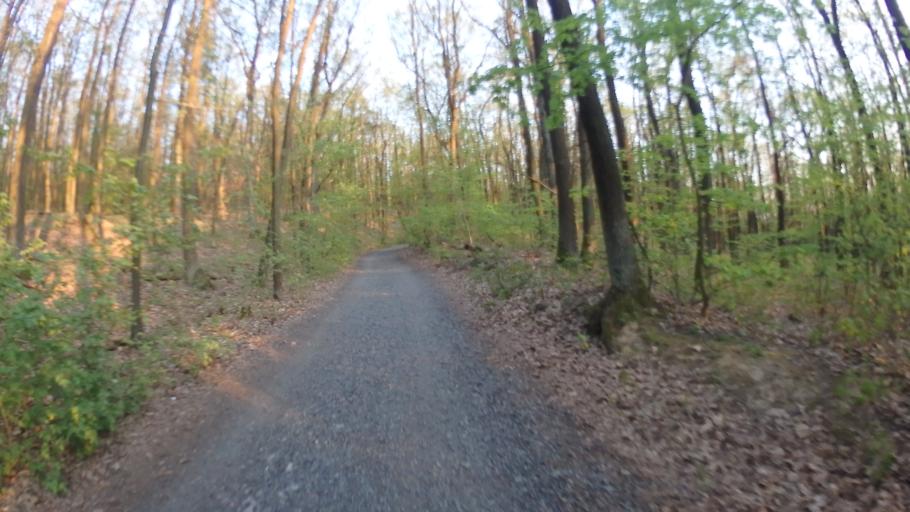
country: CZ
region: South Moravian
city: Troubsko
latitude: 49.1921
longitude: 16.5150
